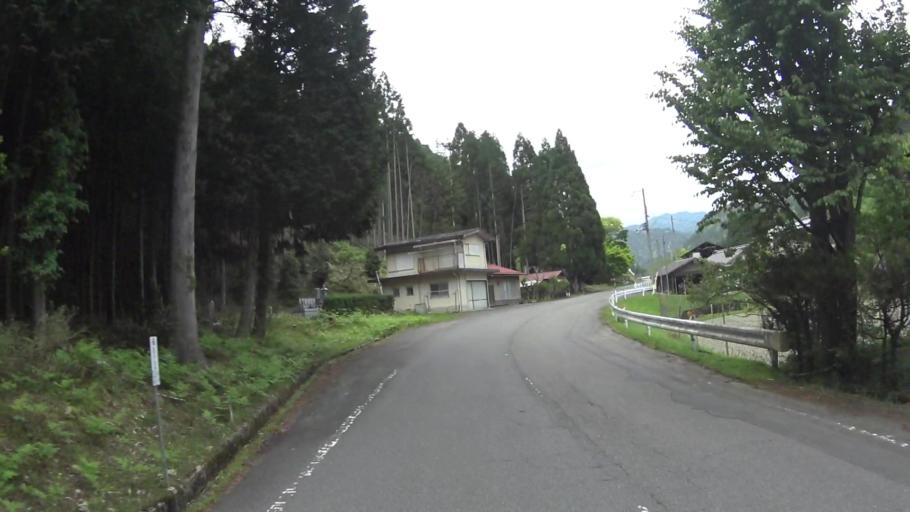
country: JP
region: Kyoto
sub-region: Kyoto-shi
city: Kamigyo-ku
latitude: 35.2055
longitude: 135.6992
